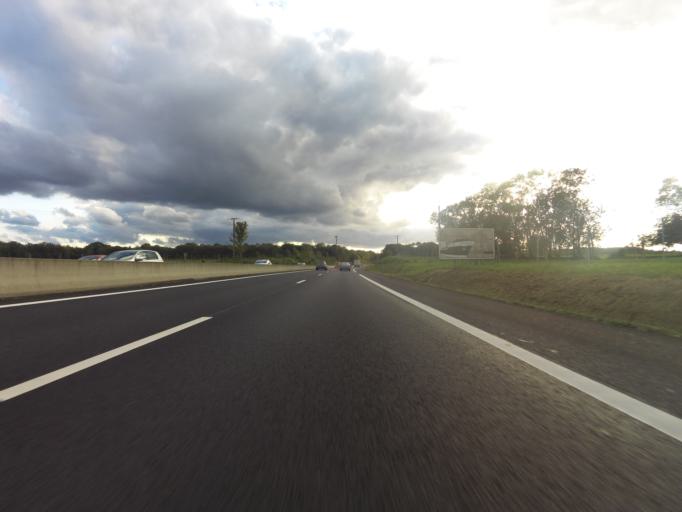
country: FR
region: Haute-Normandie
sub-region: Departement de la Seine-Maritime
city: Quincampoix
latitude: 49.5178
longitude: 1.1959
